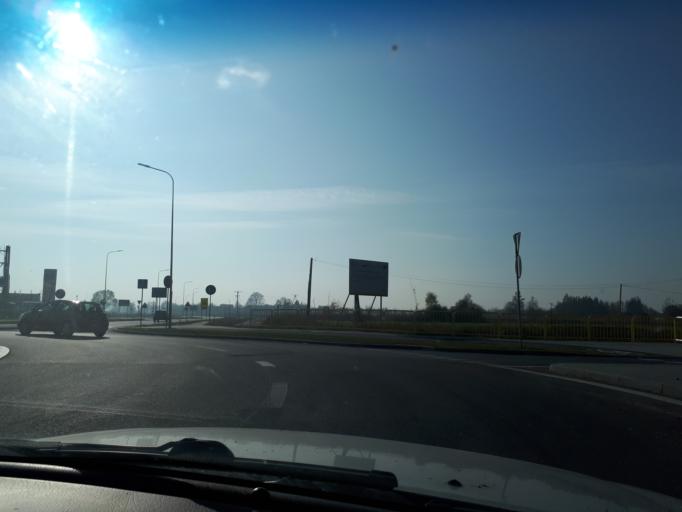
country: PL
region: Subcarpathian Voivodeship
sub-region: Powiat debicki
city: Zyrakow
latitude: 50.0762
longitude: 21.3826
